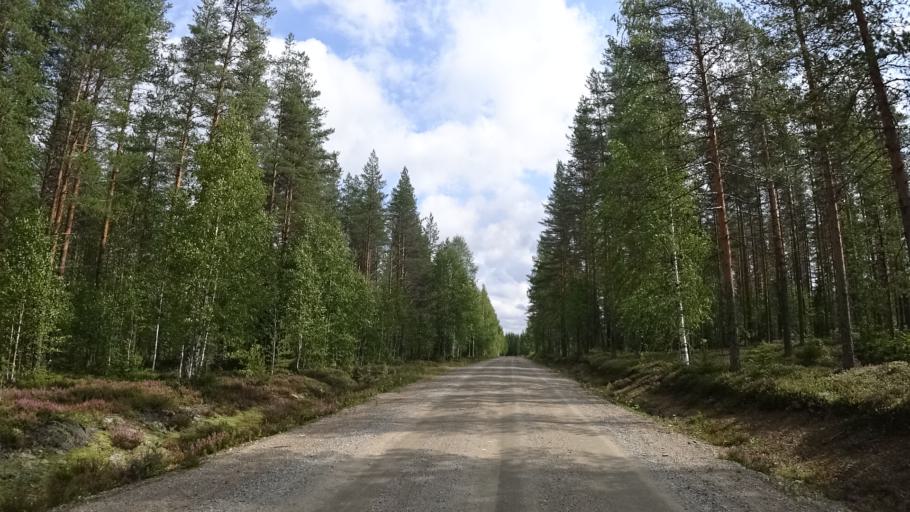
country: FI
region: North Karelia
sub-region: Joensuu
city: Ilomantsi
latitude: 62.9267
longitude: 31.3837
